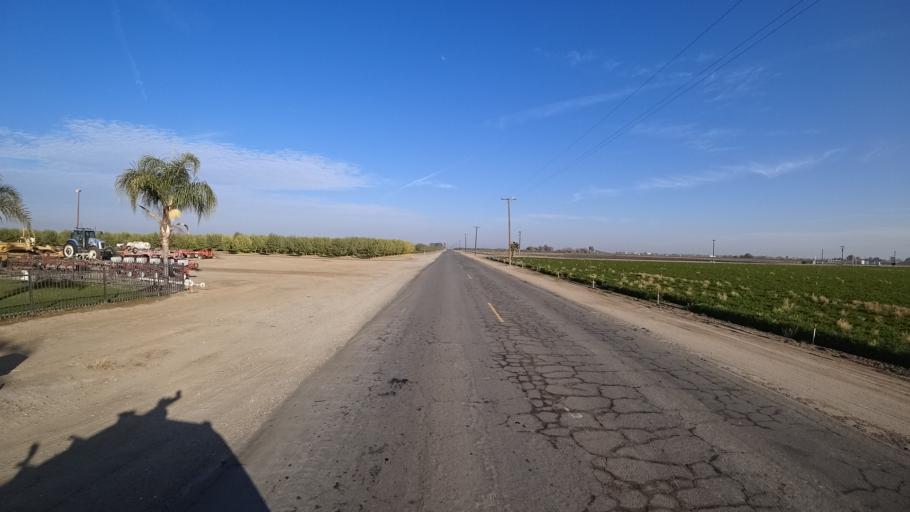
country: US
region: California
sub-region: Kern County
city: Greenfield
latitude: 35.2588
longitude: -119.0921
